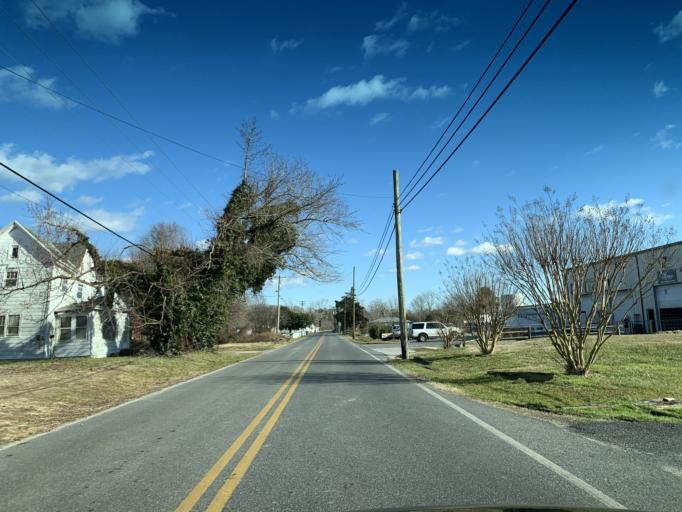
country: US
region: Maryland
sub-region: Worcester County
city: Ocean Pines
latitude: 38.3491
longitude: -75.1746
